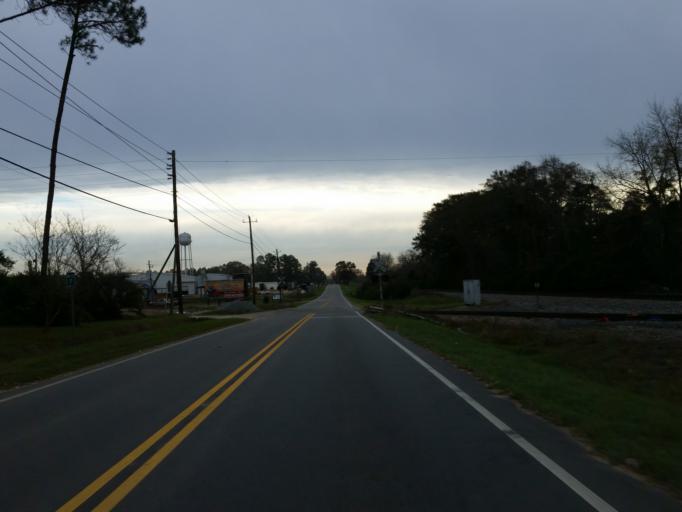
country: US
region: Georgia
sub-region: Turner County
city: Ashburn
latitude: 31.6819
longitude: -83.6414
